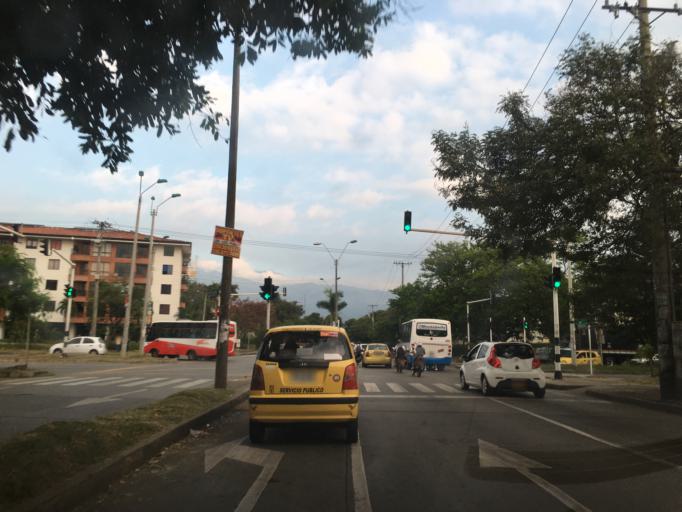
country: CO
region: Valle del Cauca
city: Cali
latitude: 3.4025
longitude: -76.5271
